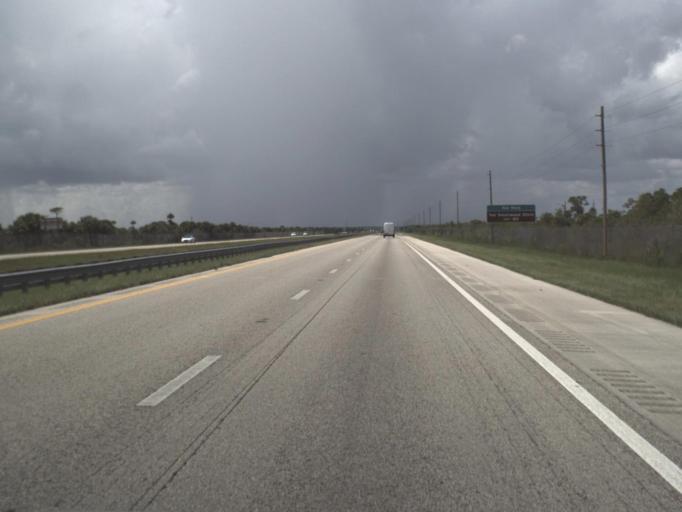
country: US
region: Florida
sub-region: Collier County
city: Immokalee
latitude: 26.1551
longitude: -81.3274
